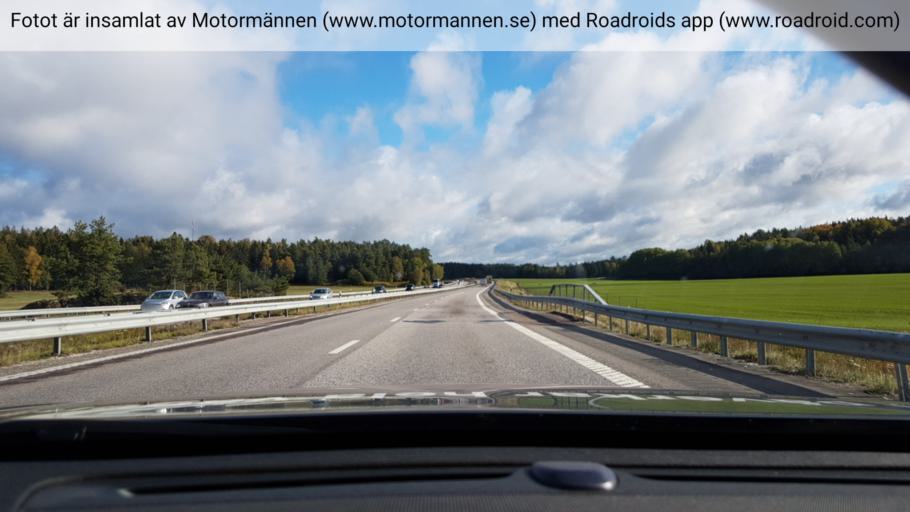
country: SE
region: Stockholm
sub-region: Sodertalje Kommun
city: Pershagen
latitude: 59.1171
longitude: 17.6163
